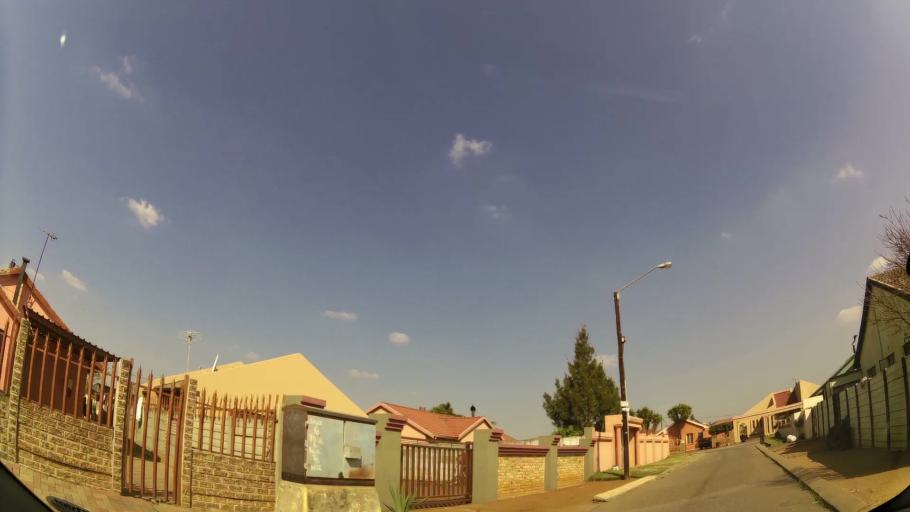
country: ZA
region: Gauteng
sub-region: Ekurhuleni Metropolitan Municipality
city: Benoni
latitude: -26.1452
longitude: 28.4040
